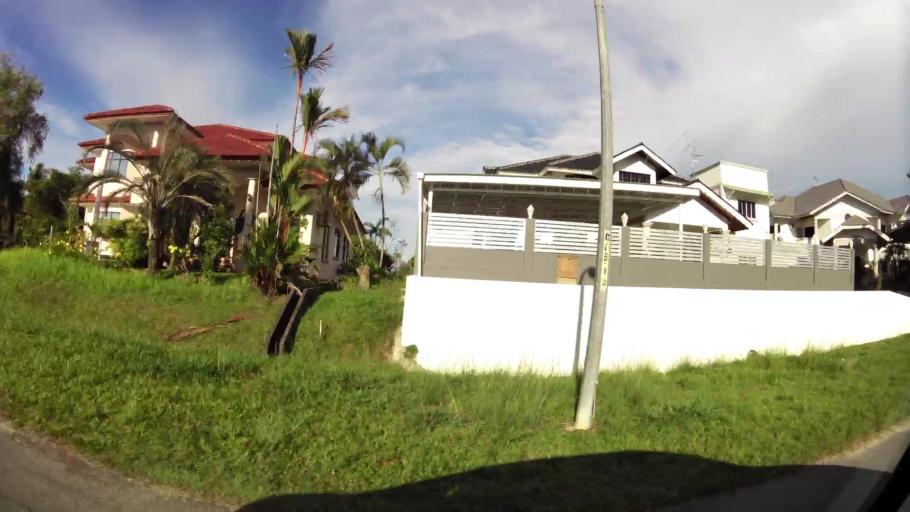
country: BN
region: Brunei and Muara
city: Bandar Seri Begawan
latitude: 4.9860
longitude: 114.9706
